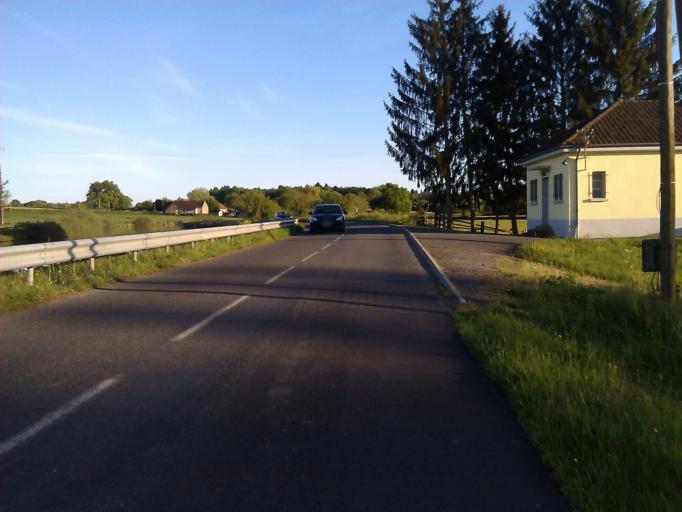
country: FR
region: Bourgogne
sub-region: Departement de Saone-et-Loire
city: Palinges
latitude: 46.5476
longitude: 4.2102
